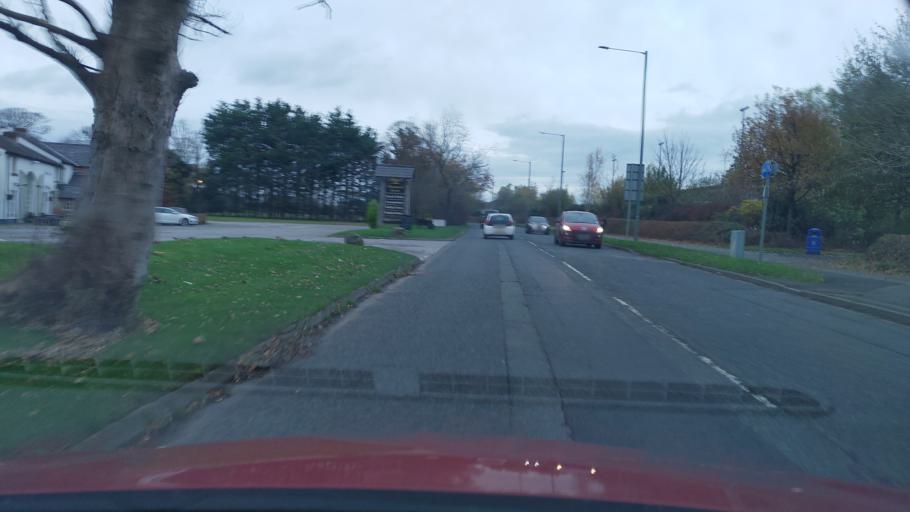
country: GB
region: England
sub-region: Lancashire
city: Euxton
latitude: 53.6828
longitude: -2.6765
